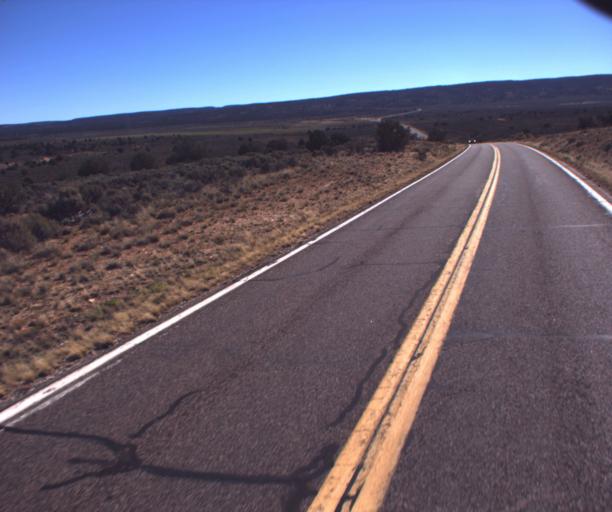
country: US
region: Arizona
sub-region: Coconino County
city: Fredonia
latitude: 36.8595
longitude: -112.3091
